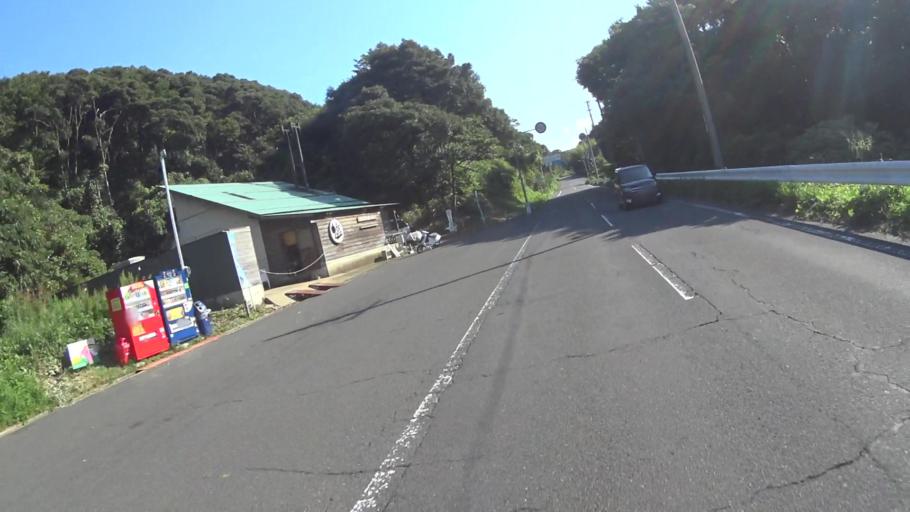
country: JP
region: Kyoto
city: Miyazu
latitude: 35.7077
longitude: 135.0694
